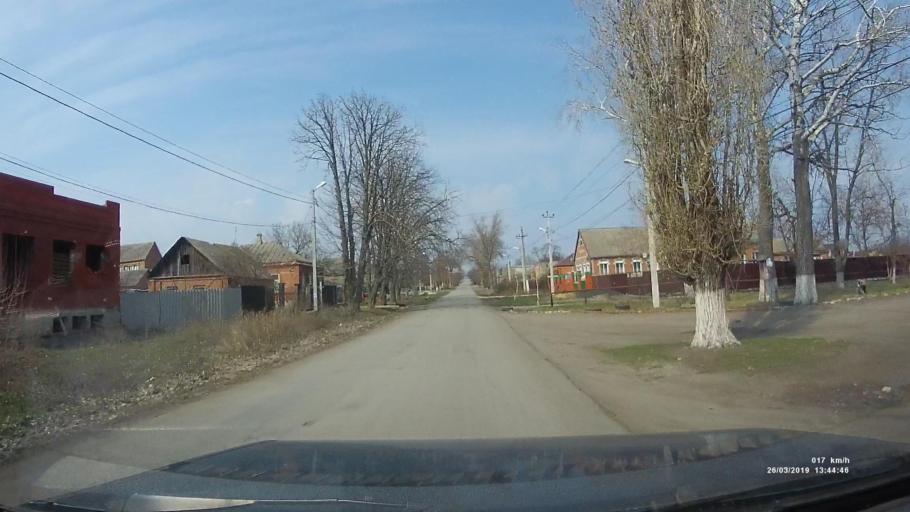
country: RU
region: Rostov
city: Novobessergenovka
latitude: 47.1830
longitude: 38.8426
